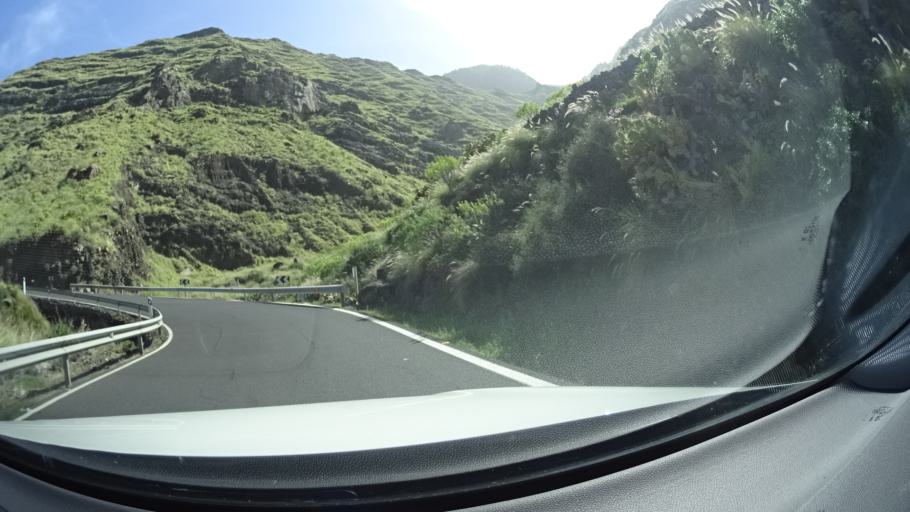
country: ES
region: Canary Islands
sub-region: Provincia de Las Palmas
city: Agaete
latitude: 28.0700
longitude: -15.7115
